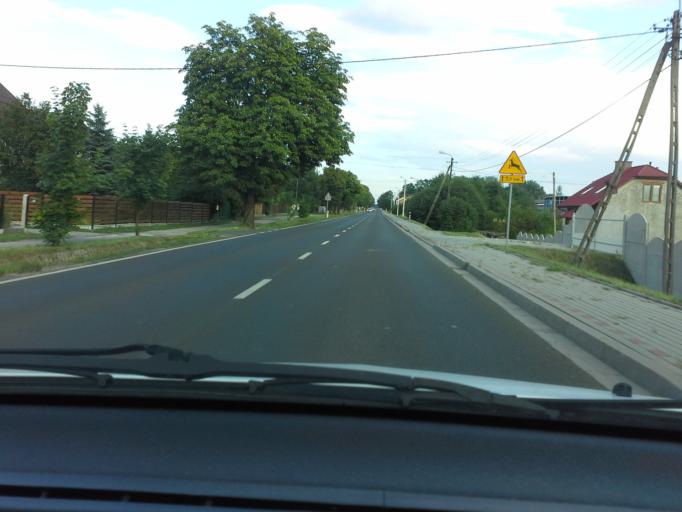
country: PL
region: Lesser Poland Voivodeship
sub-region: Powiat chrzanowski
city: Trzebinia
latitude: 50.1473
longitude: 19.5001
